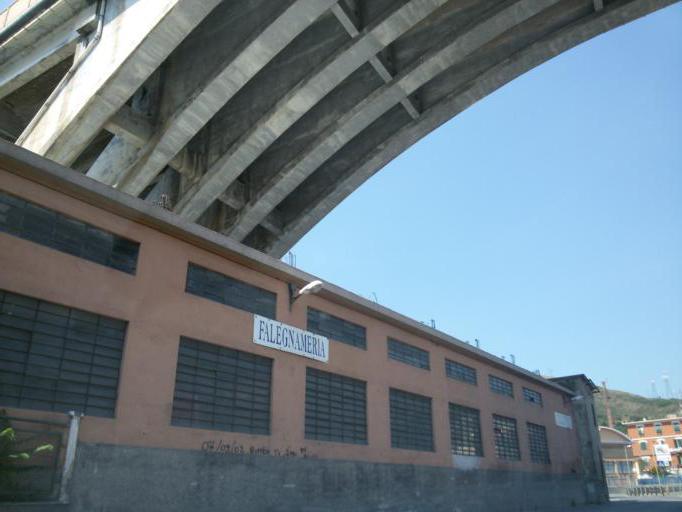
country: IT
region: Liguria
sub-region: Provincia di Genova
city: San Teodoro
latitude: 44.4288
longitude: 8.8580
